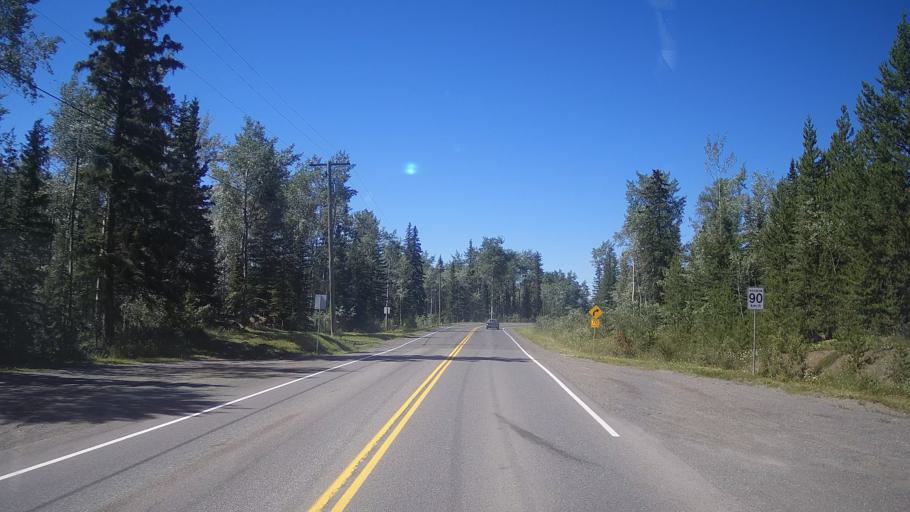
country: CA
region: British Columbia
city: Cache Creek
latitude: 51.5541
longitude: -121.2214
